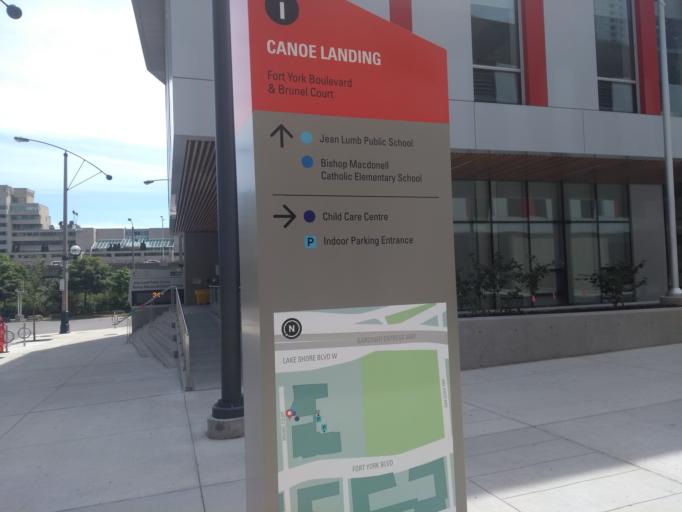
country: CA
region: Ontario
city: Toronto
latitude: 43.6396
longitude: -79.3943
